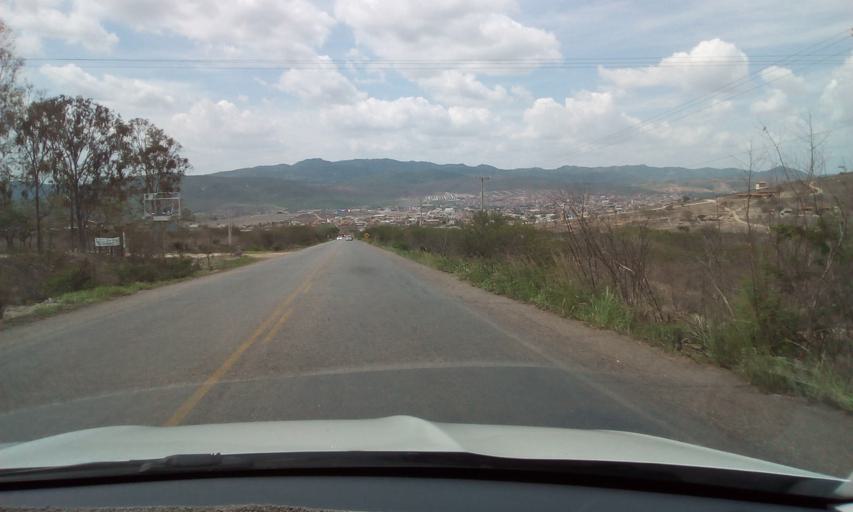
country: BR
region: Pernambuco
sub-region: Bezerros
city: Bezerros
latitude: -8.2651
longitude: -35.7545
